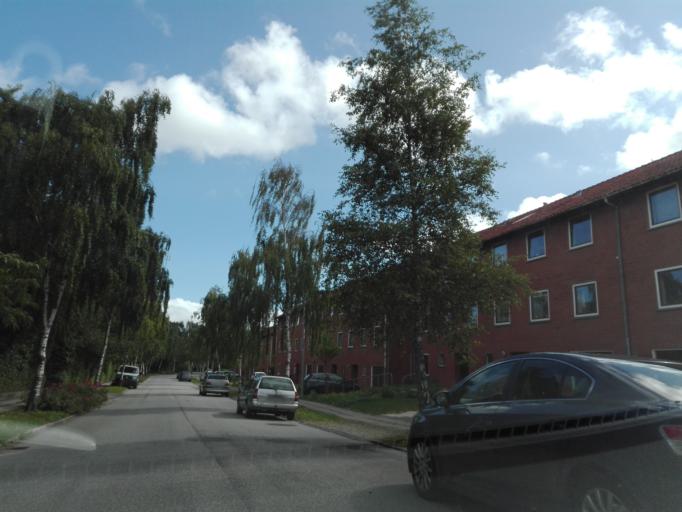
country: DK
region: Central Jutland
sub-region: Arhus Kommune
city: Arhus
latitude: 56.1157
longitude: 10.1910
